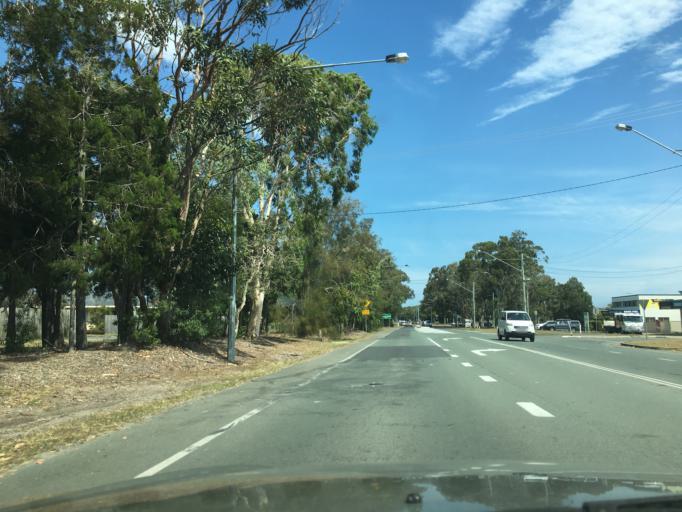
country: AU
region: Queensland
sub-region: Moreton Bay
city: Bongaree
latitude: -27.0723
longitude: 153.1628
